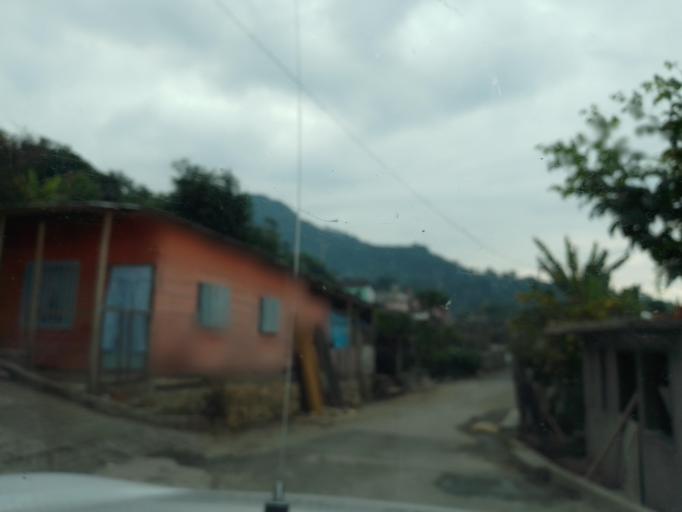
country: MX
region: Chiapas
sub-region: Union Juarez
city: Santo Domingo
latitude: 15.0533
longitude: -92.1241
